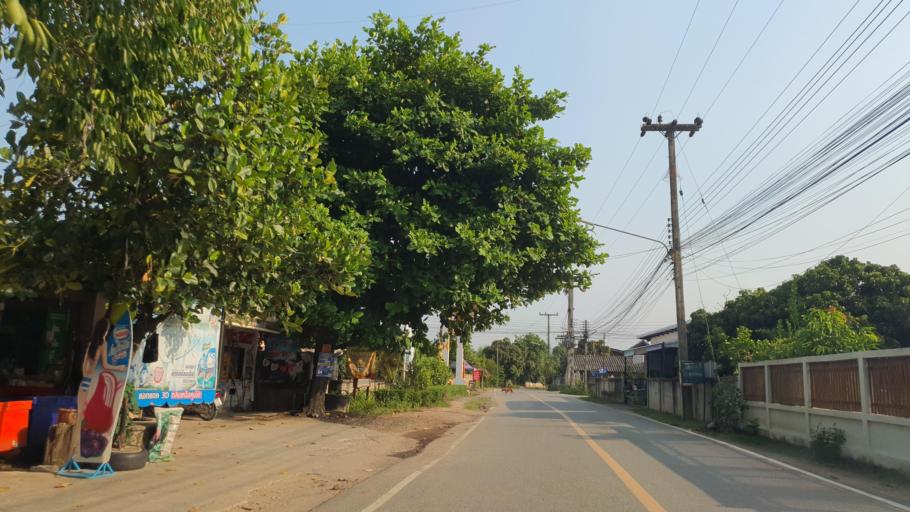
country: TH
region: Chiang Mai
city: Mae Wang
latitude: 18.6607
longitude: 98.8187
